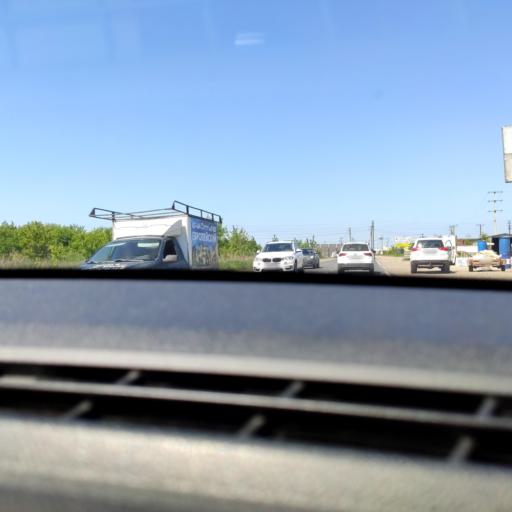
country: RU
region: Samara
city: Podstepki
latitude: 53.5231
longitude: 49.1984
